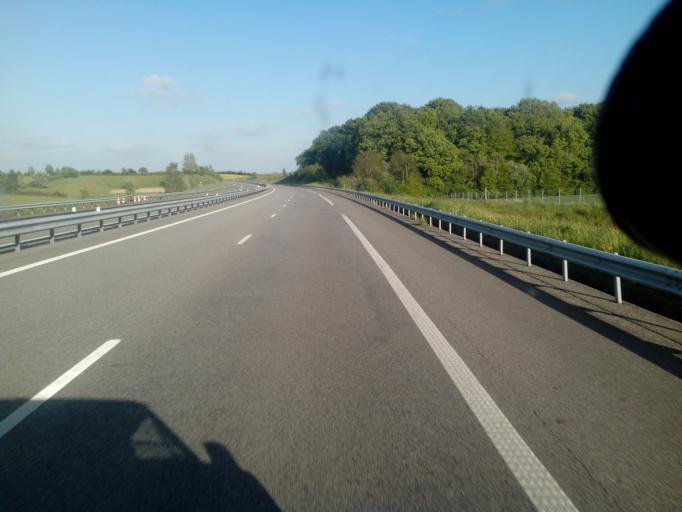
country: FR
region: Haute-Normandie
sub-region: Departement de la Seine-Maritime
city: Limesy
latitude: 49.6469
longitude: 0.9616
